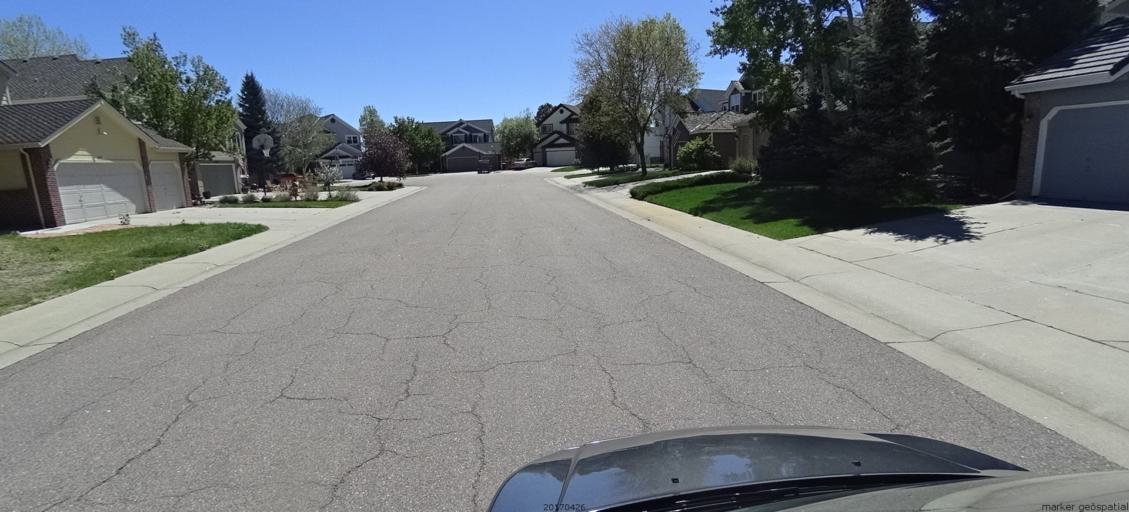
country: US
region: Colorado
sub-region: Adams County
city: Lone Tree
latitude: 39.5467
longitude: -104.8947
